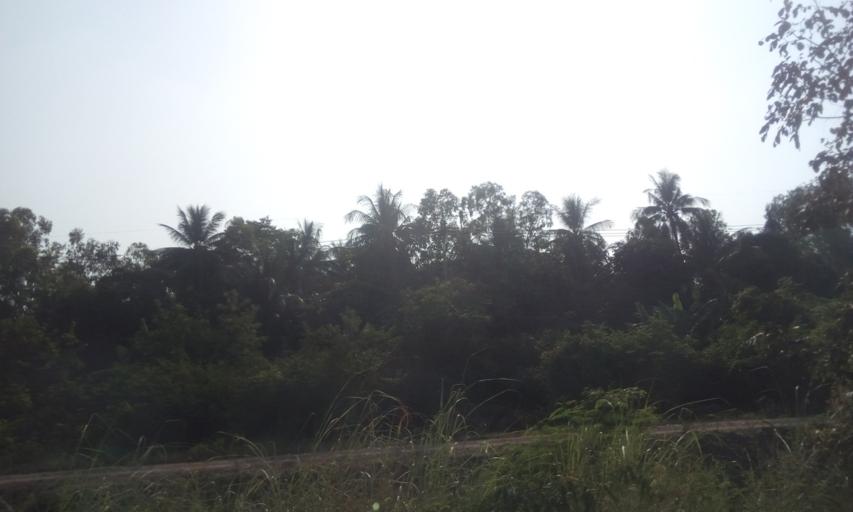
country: TH
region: Sing Buri
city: Phrom Buri
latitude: 14.7512
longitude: 100.4399
